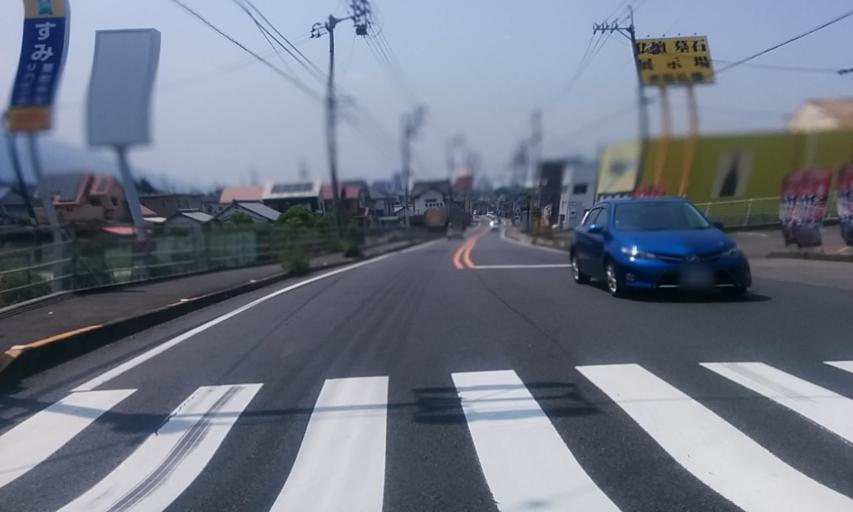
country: JP
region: Ehime
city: Niihama
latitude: 33.9343
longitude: 133.2938
